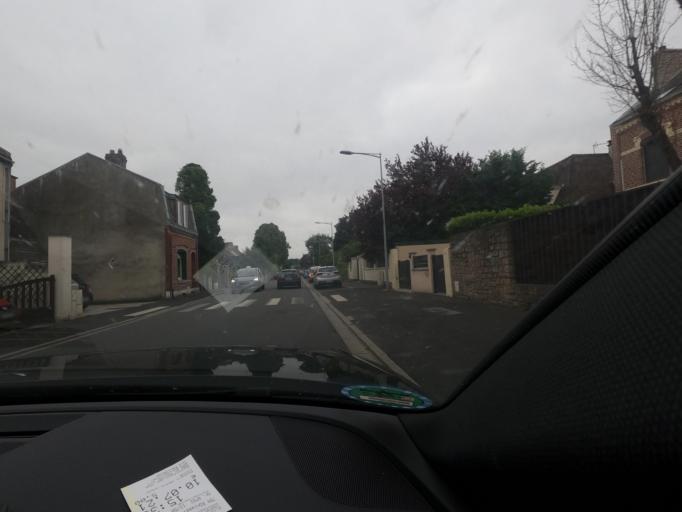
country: FR
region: Picardie
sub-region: Departement de la Somme
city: Amiens
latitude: 49.8735
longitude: 2.3066
